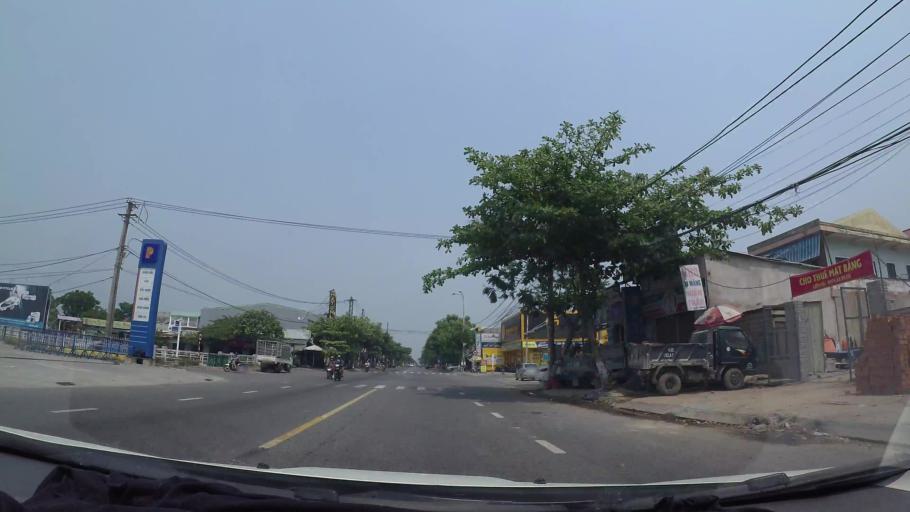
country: VN
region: Da Nang
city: Cam Le
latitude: 15.9823
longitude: 108.2081
